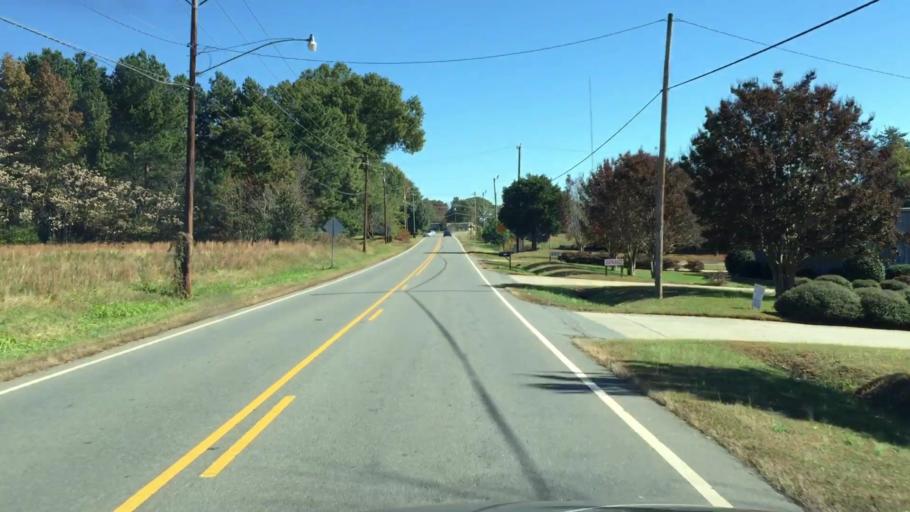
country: US
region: North Carolina
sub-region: Rockingham County
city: Reidsville
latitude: 36.3268
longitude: -79.6345
